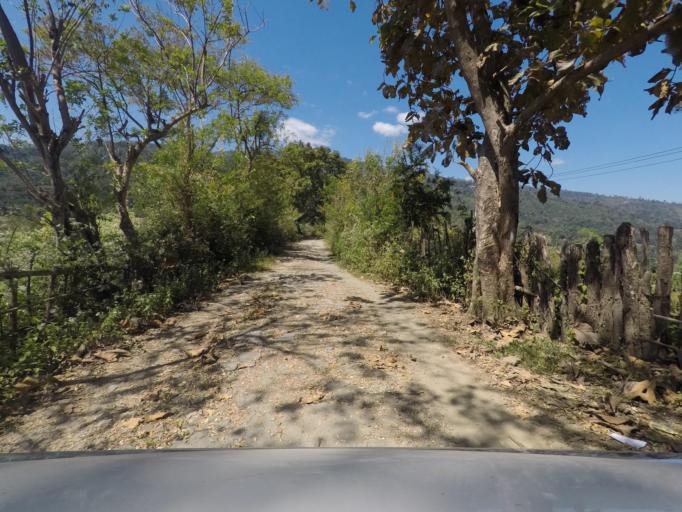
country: TL
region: Ermera
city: Gleno
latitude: -8.7183
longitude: 125.2996
